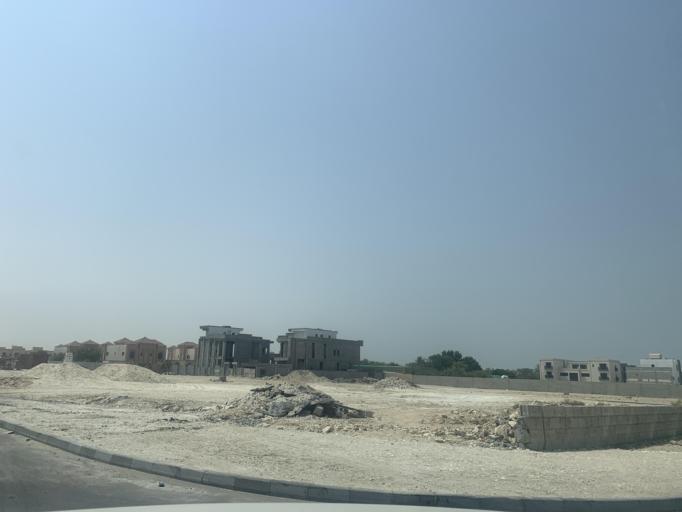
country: BH
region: Central Governorate
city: Madinat Hamad
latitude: 26.1490
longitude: 50.4756
